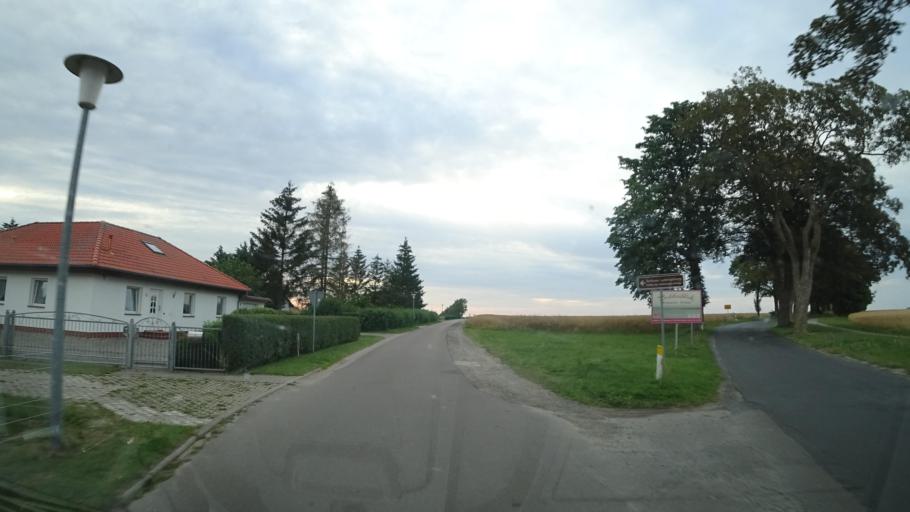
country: DE
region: Mecklenburg-Vorpommern
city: Kemnitz
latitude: 54.0888
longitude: 13.5323
